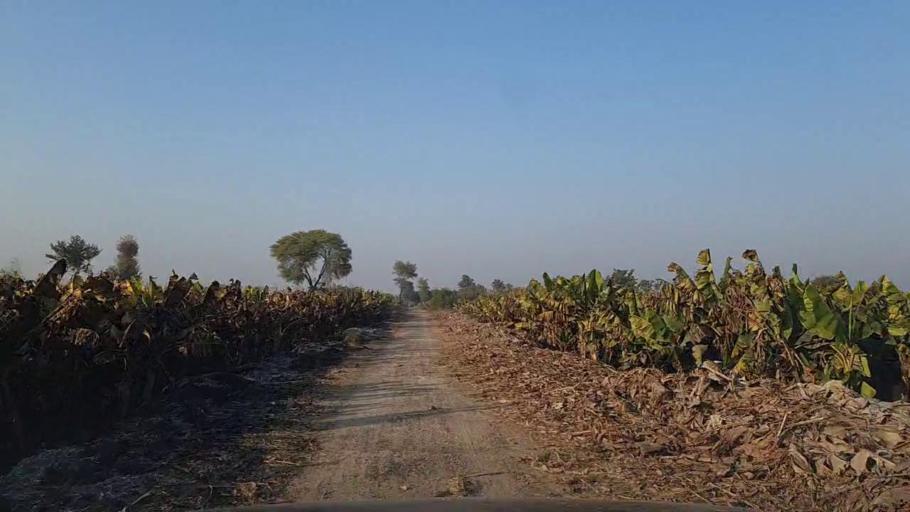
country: PK
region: Sindh
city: Daur
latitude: 26.4637
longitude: 68.3880
